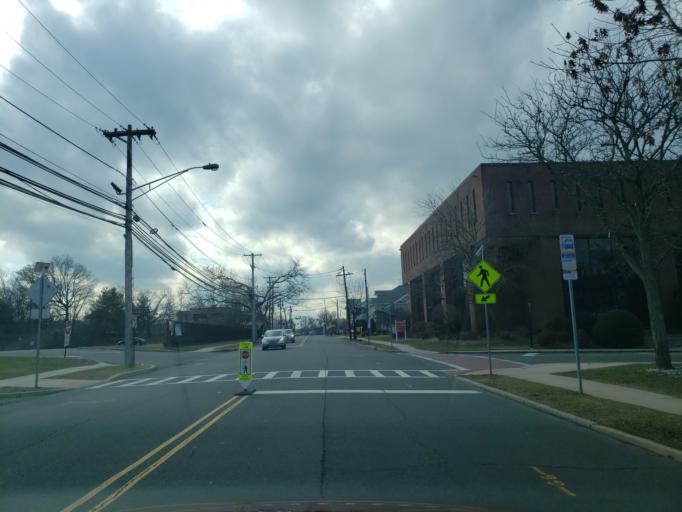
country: US
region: New Jersey
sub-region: Union County
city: Springfield
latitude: 40.7074
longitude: -74.3149
